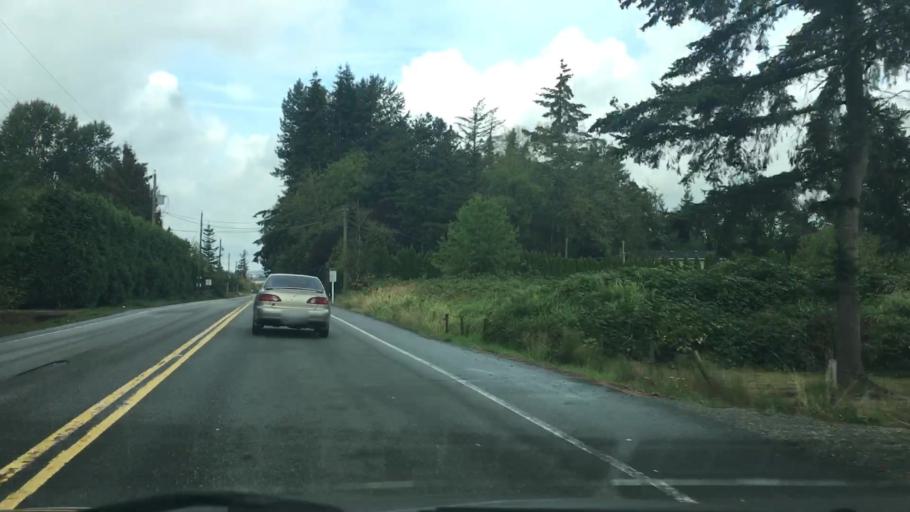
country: CA
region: British Columbia
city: Langley
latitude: 49.1045
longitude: -122.6047
